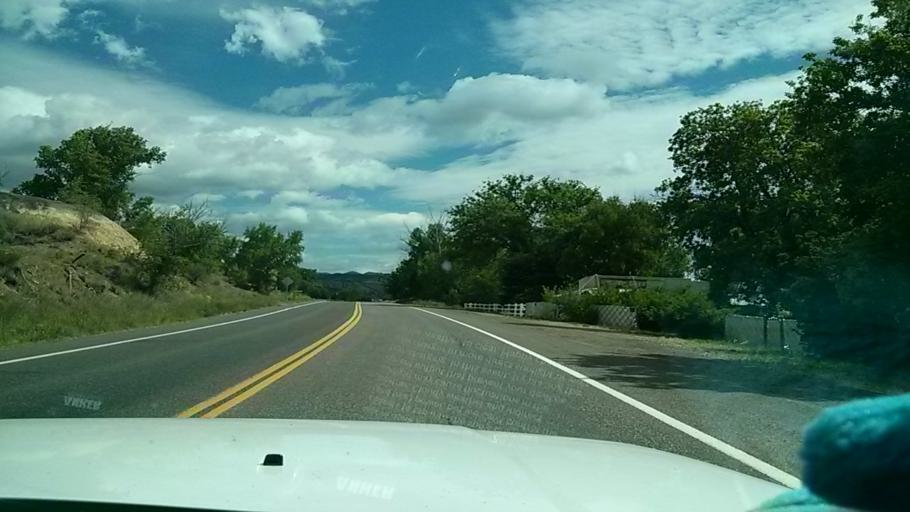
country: US
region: Utah
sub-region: Kane County
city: Kanab
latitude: 37.2491
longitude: -112.6626
